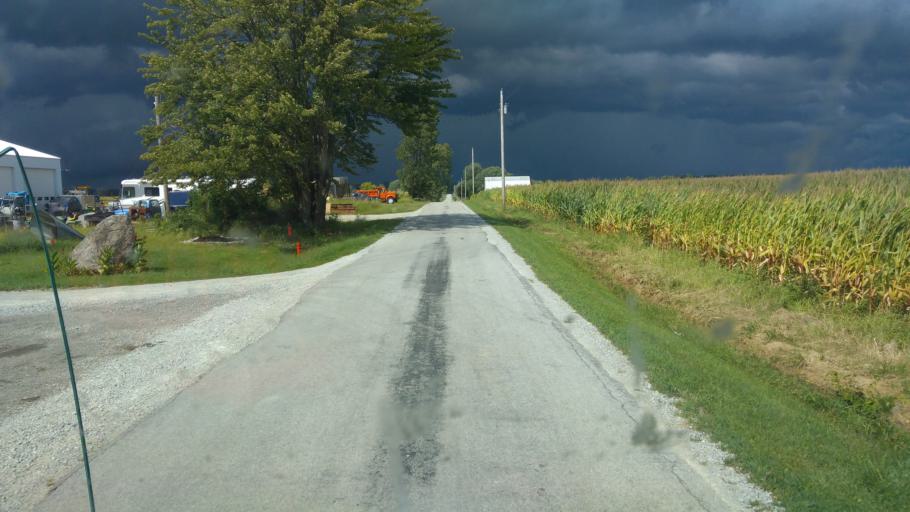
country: US
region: Ohio
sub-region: Hardin County
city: Kenton
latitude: 40.6334
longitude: -83.5156
